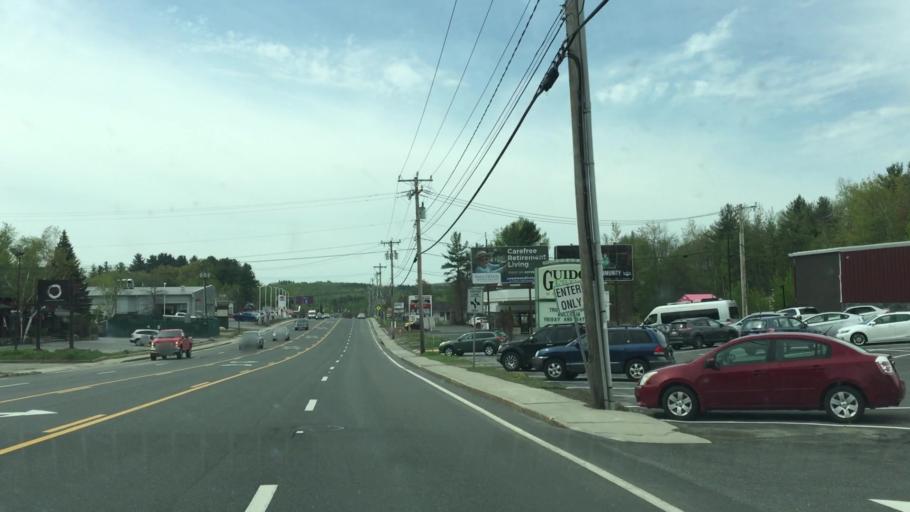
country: US
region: Massachusetts
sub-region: Berkshire County
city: Pittsfield
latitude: 42.4087
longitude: -73.2635
